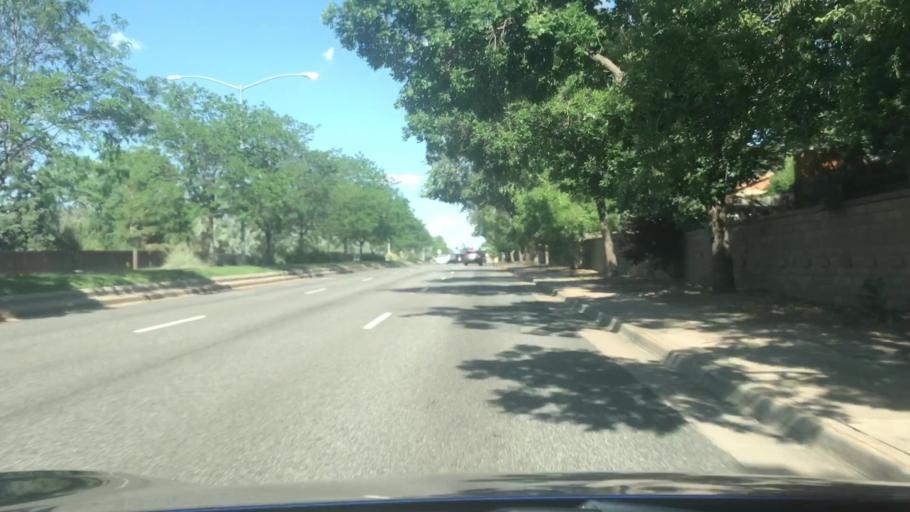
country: US
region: Colorado
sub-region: Arapahoe County
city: Dove Valley
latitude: 39.6530
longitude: -104.7950
